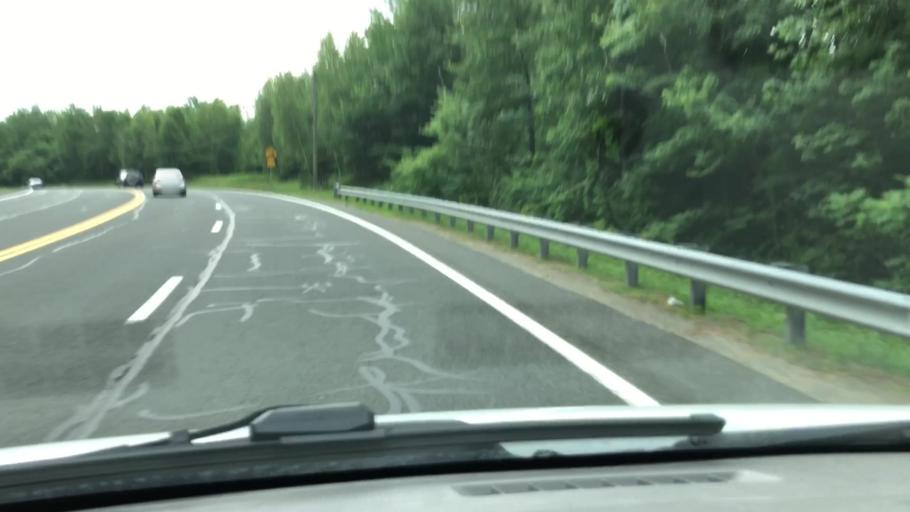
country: US
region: Massachusetts
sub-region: Berkshire County
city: Lanesborough
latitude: 42.4952
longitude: -73.2244
